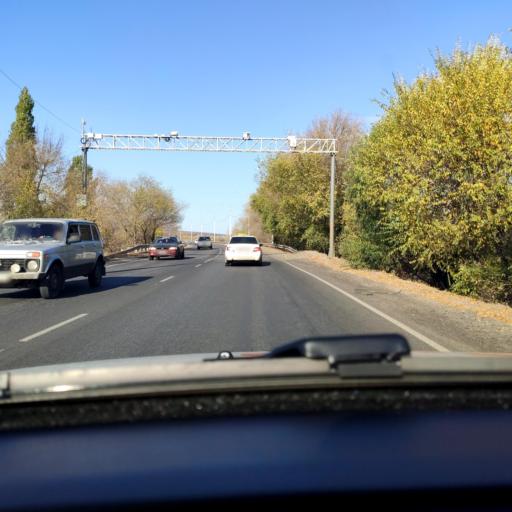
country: RU
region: Voronezj
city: Pridonskoy
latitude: 51.7132
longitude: 39.0747
